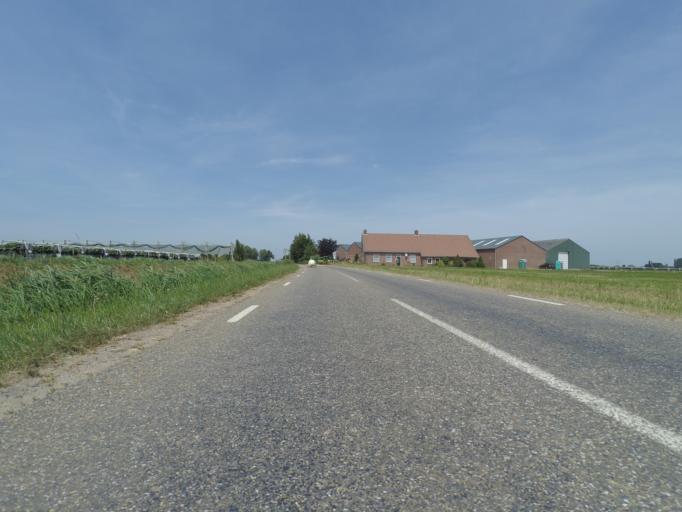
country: NL
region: North Brabant
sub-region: Gemeente Steenbergen
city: Kruisland
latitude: 51.5441
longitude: 4.3752
